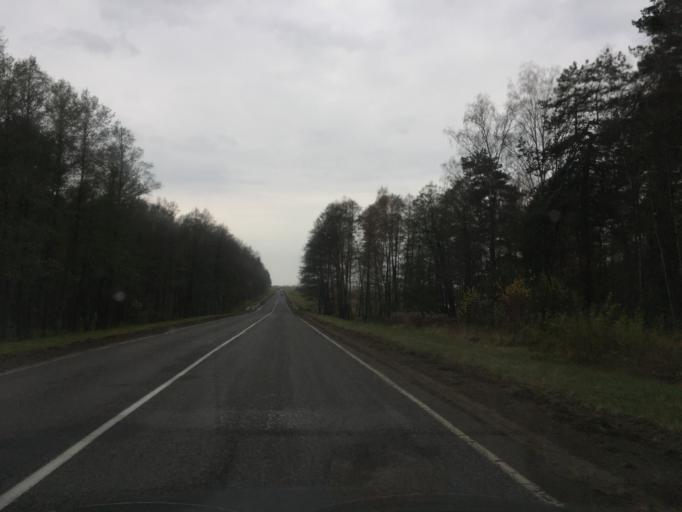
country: BY
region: Gomel
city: Dowsk
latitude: 53.1922
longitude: 30.5089
